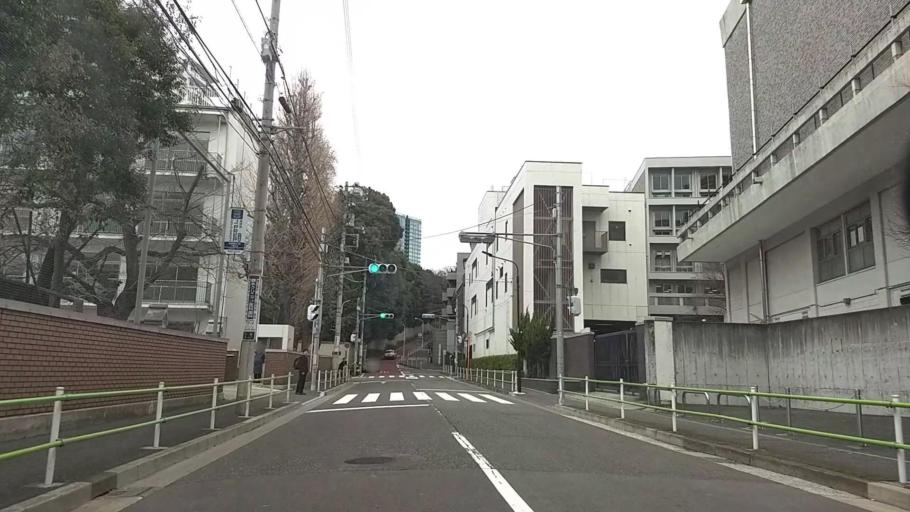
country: JP
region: Tokyo
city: Tokyo
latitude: 35.6489
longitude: 139.7413
